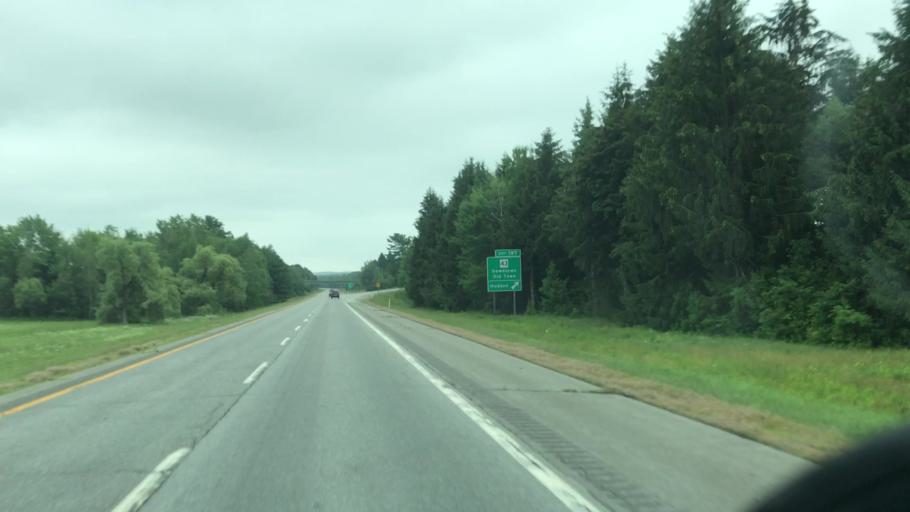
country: US
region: Maine
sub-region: Penobscot County
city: Milford
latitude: 44.9648
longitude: -68.7070
